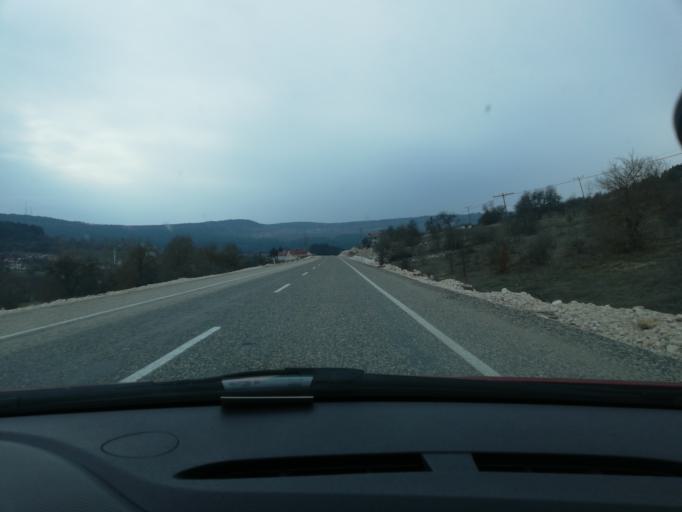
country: TR
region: Kastamonu
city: Pinarbasi
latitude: 41.5926
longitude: 33.0964
